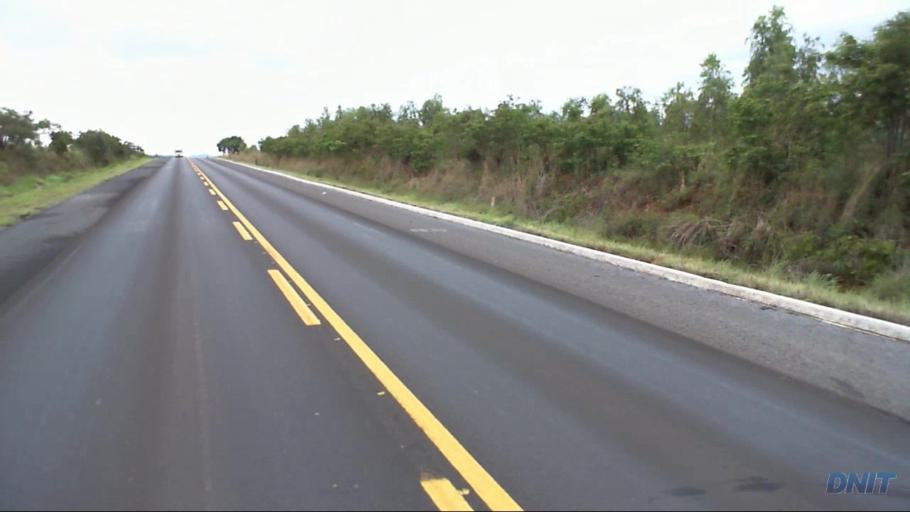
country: BR
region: Goias
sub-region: Barro Alto
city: Barro Alto
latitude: -15.2189
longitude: -48.6490
